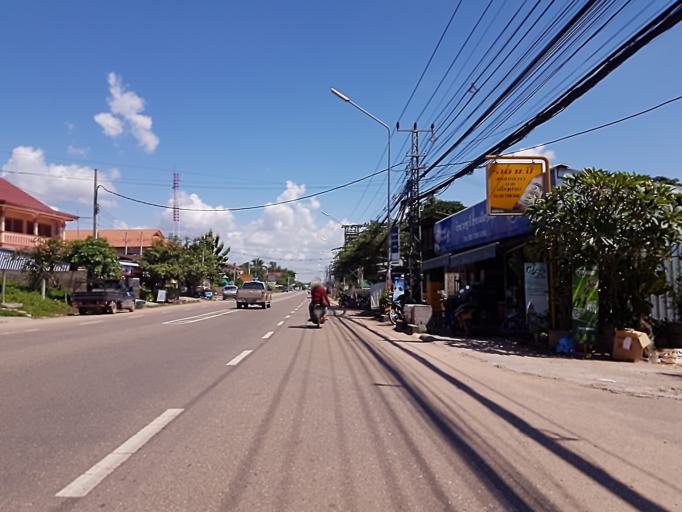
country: TH
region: Nong Khai
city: Tha Bo
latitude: 17.8981
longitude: 102.6375
